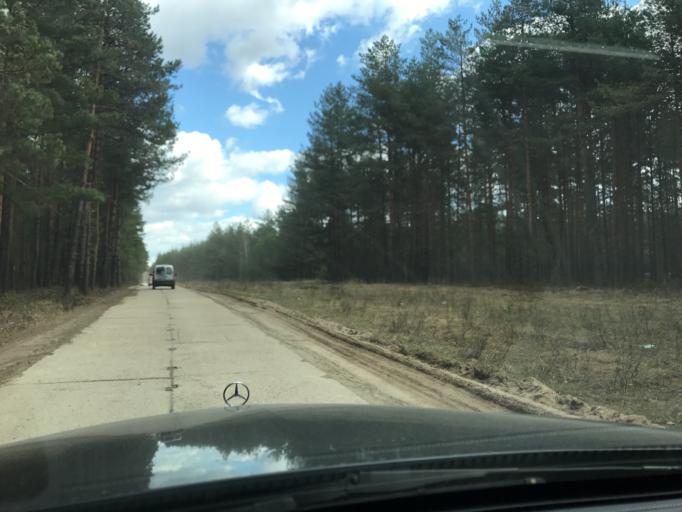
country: RU
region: Vladimir
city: Pokrov
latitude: 55.8674
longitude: 39.2298
